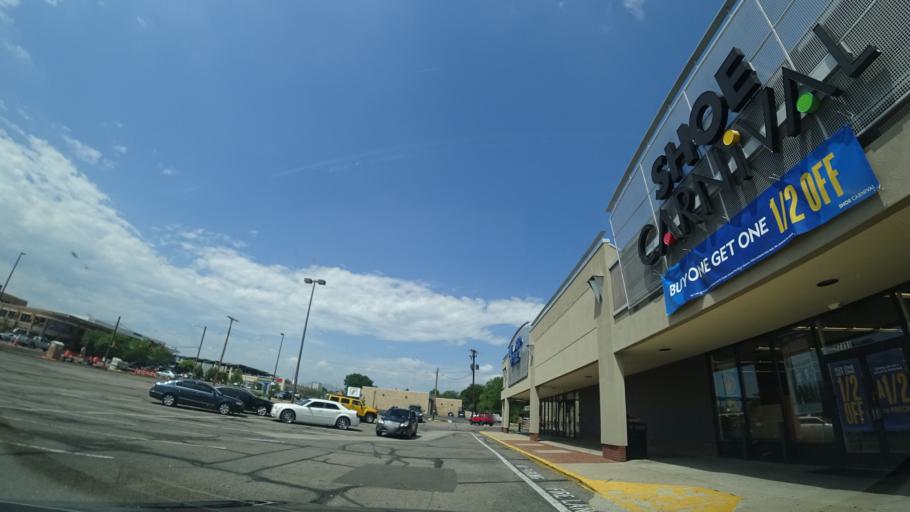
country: US
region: Colorado
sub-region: Jefferson County
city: Lakewood
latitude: 39.7118
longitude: -105.0760
